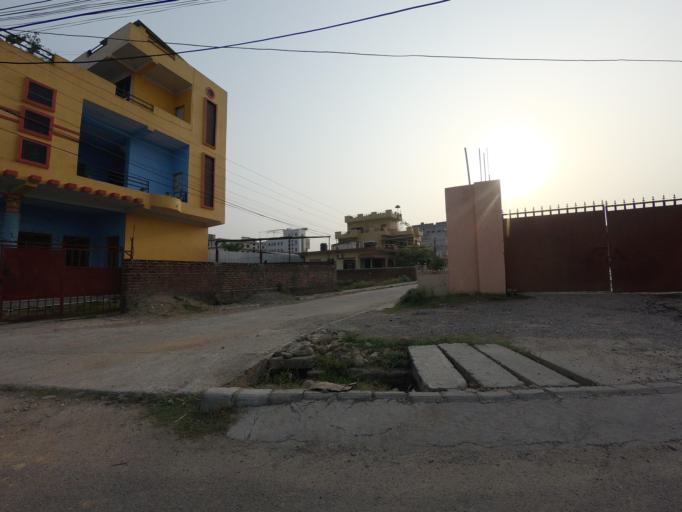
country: NP
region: Western Region
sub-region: Lumbini Zone
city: Bhairahawa
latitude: 27.5118
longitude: 83.4608
